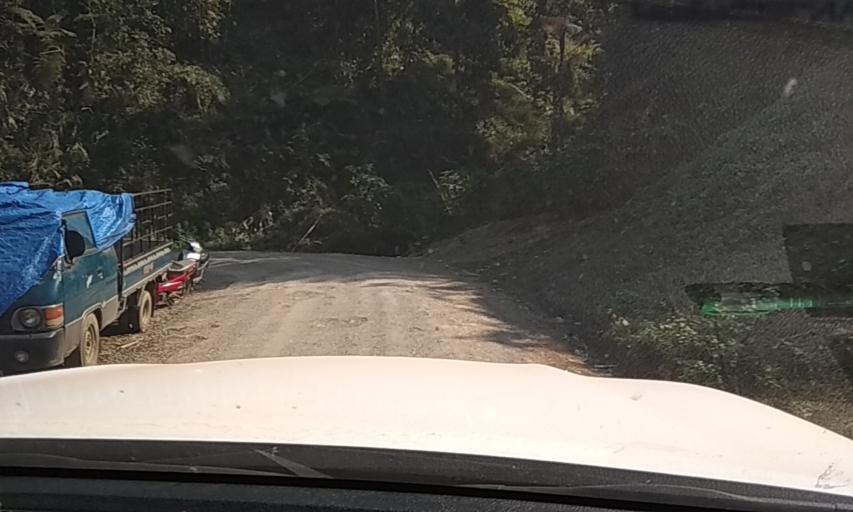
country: LA
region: Phongsali
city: Phongsali
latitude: 21.6611
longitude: 102.0901
